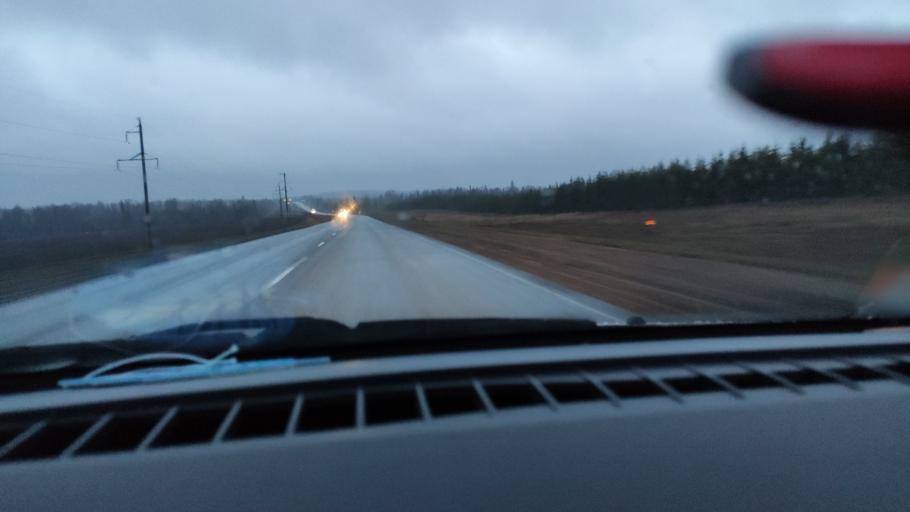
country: RU
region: Udmurtiya
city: Alnashi
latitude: 56.2719
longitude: 52.3638
